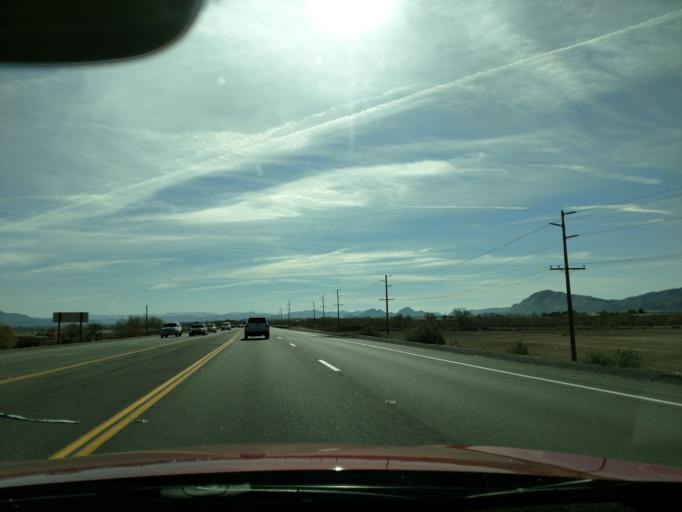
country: US
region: California
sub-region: Riverside County
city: San Jacinto
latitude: 33.8383
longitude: -117.0036
